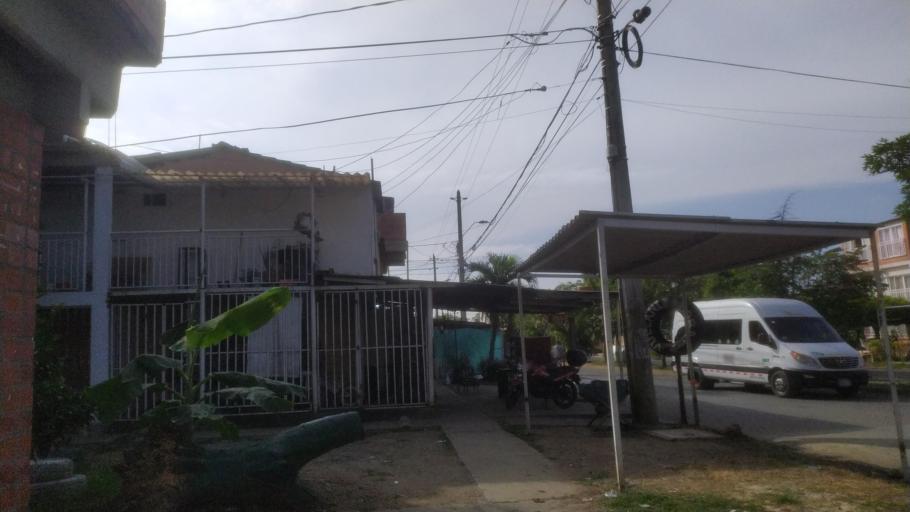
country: CO
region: Valle del Cauca
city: Jamundi
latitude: 3.2396
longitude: -76.5108
